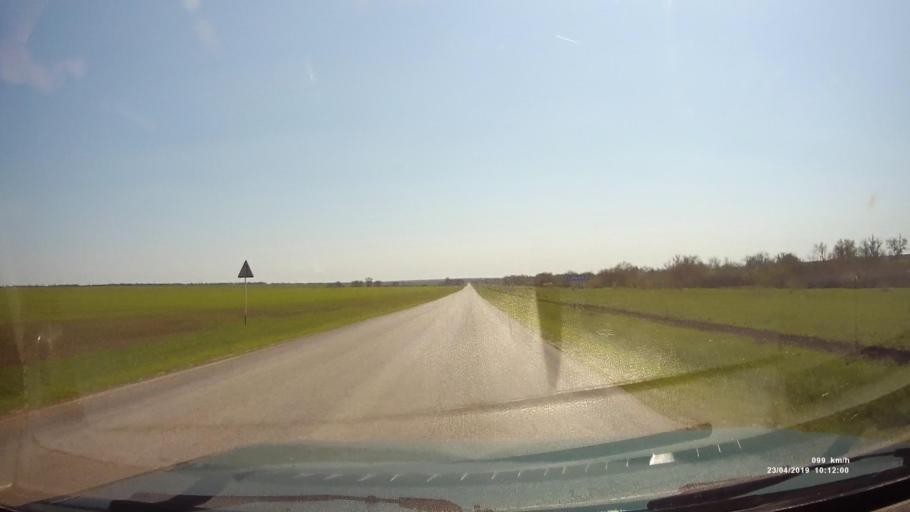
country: RU
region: Rostov
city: Sovetskoye
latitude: 46.6921
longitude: 42.3285
